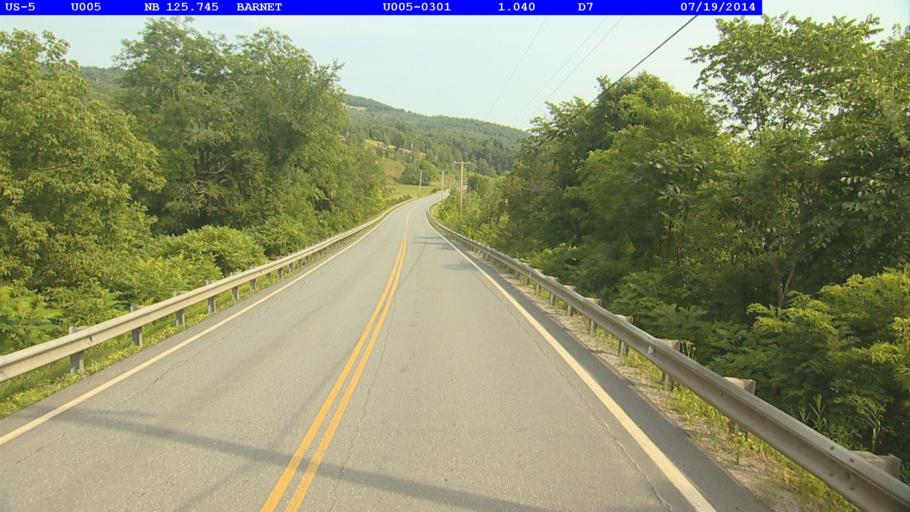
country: US
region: New Hampshire
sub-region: Grafton County
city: Woodsville
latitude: 44.2702
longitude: -72.0688
